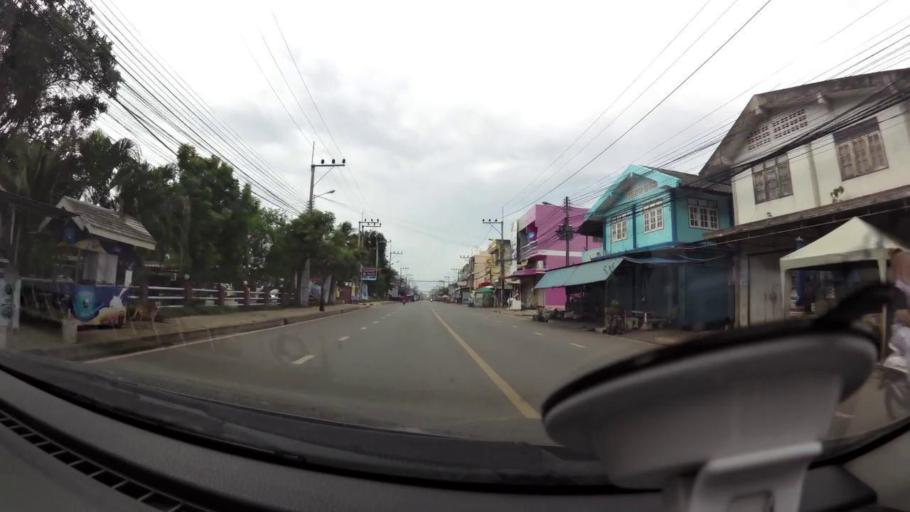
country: TH
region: Prachuap Khiri Khan
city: Pran Buri
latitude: 12.3990
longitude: 99.9904
